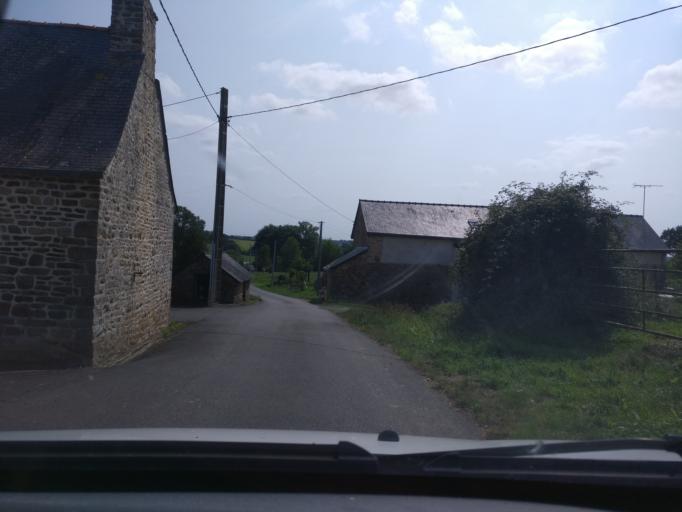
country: FR
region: Brittany
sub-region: Departement d'Ille-et-Vilaine
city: Gosne
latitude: 48.2613
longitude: -1.4799
